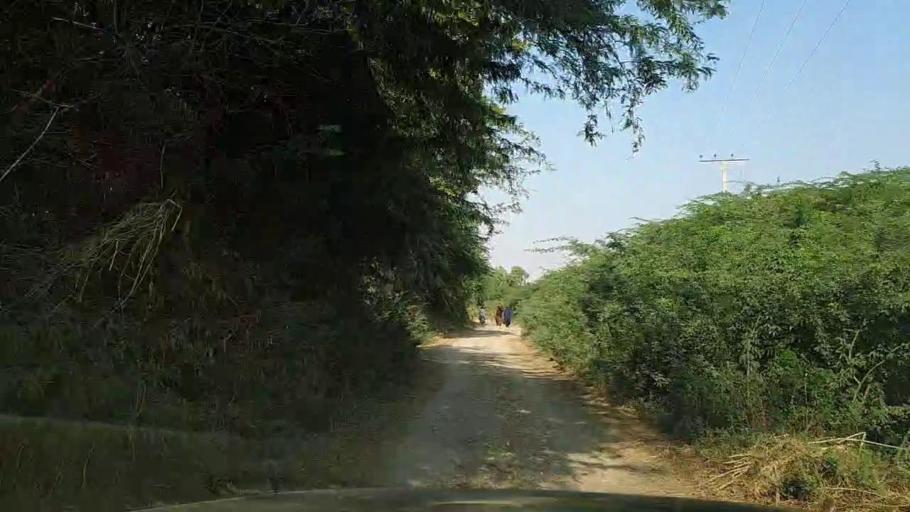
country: PK
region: Sindh
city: Thatta
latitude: 24.7963
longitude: 67.8227
